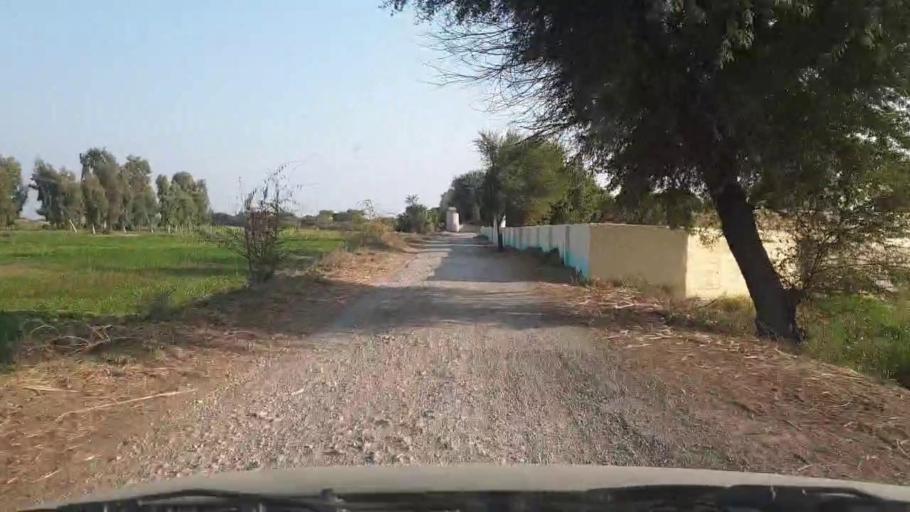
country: PK
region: Sindh
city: Samaro
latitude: 25.2743
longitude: 69.3629
